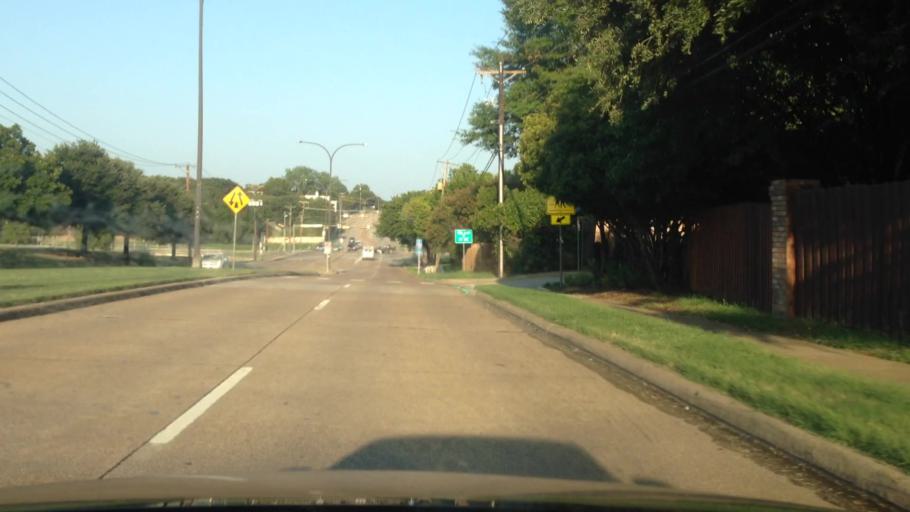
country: US
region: Texas
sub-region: Tarrant County
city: Dalworthington Gardens
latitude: 32.6823
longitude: -97.1798
